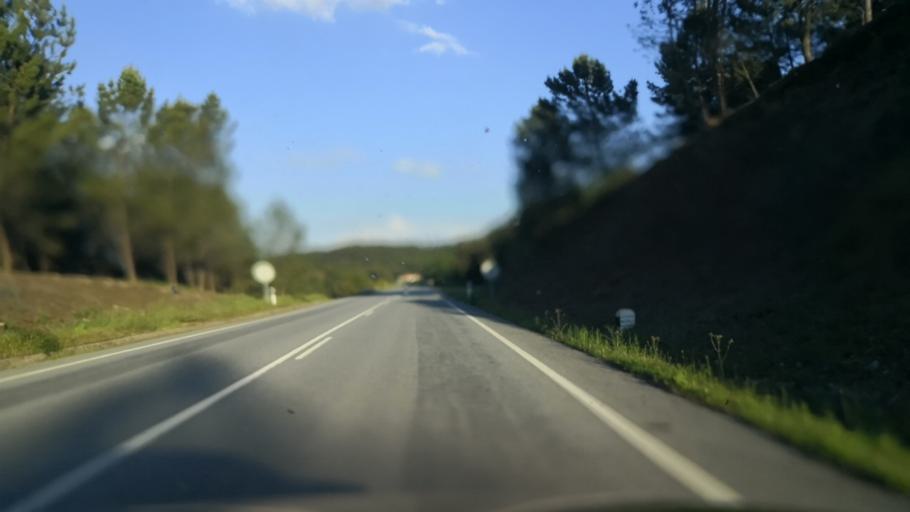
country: PT
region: Portalegre
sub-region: Marvao
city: Marvao
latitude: 39.3709
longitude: -7.3484
